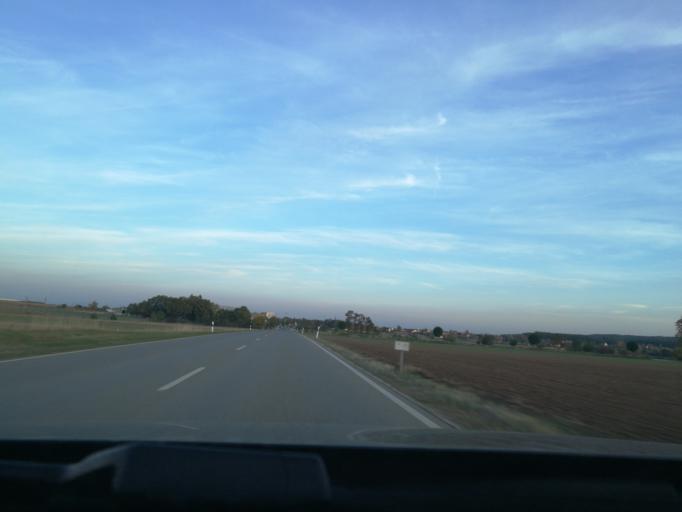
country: DE
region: Bavaria
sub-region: Regierungsbezirk Mittelfranken
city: Veitsbronn
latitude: 49.4986
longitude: 10.8990
